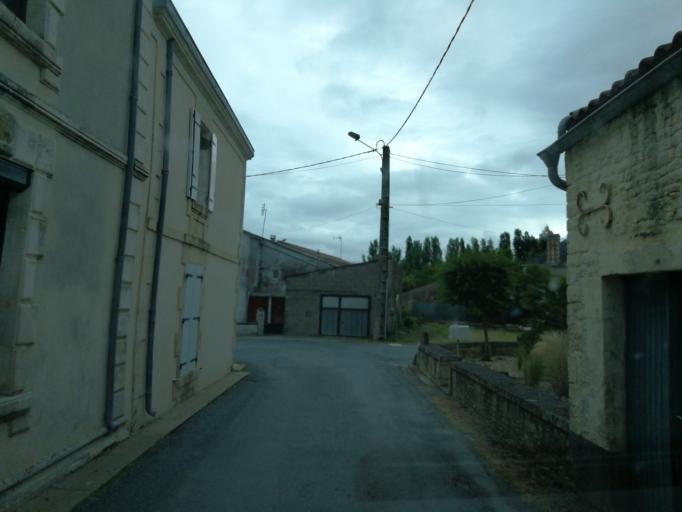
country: FR
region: Pays de la Loire
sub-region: Departement de la Vendee
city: Le Langon
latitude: 46.3748
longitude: -0.9270
